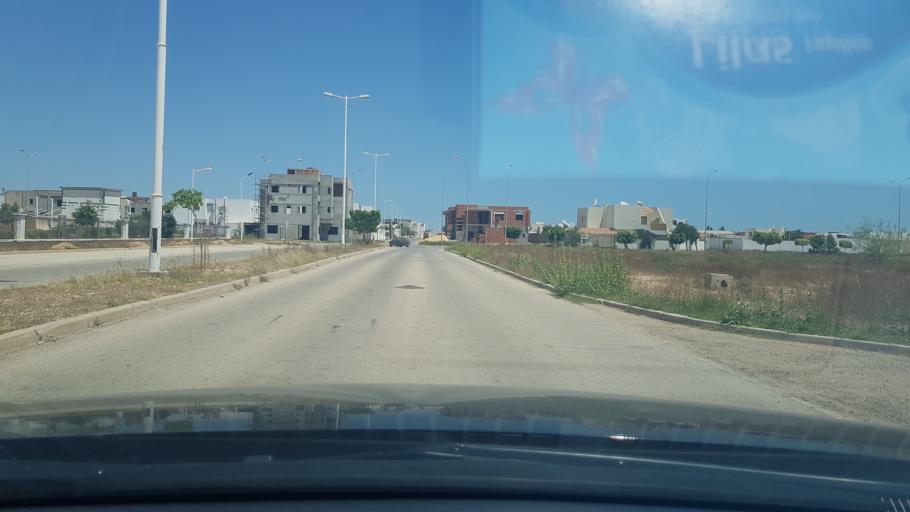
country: TN
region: Safaqis
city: Al Qarmadah
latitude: 34.8375
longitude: 10.7581
